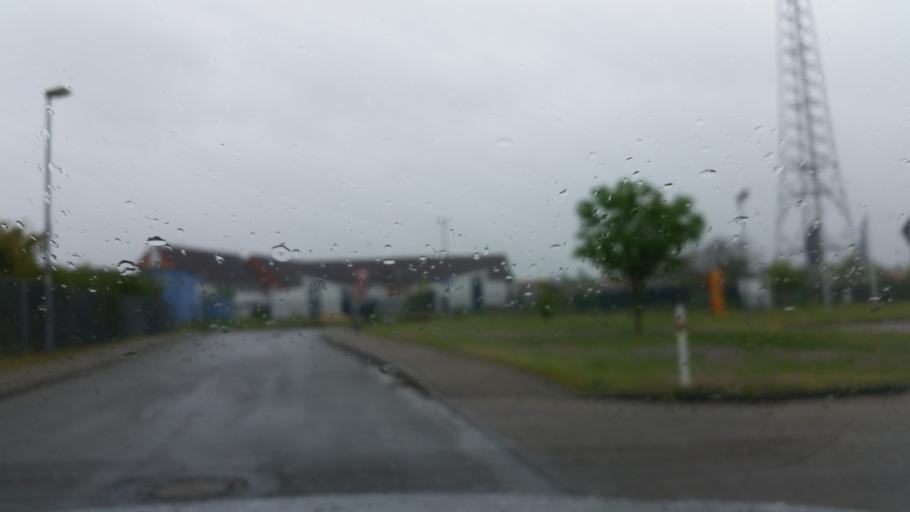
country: DE
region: Saxony-Anhalt
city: Gardelegen
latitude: 52.5378
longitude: 11.4068
